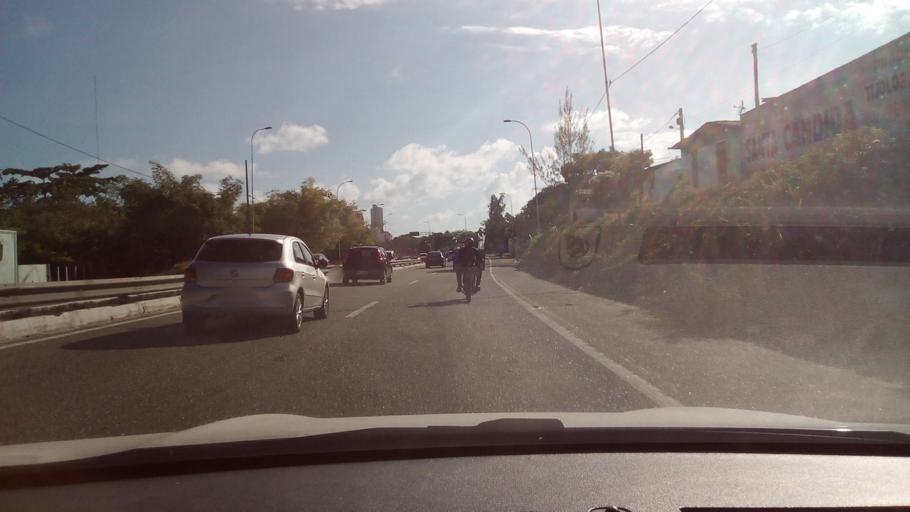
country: BR
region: Paraiba
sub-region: Joao Pessoa
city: Joao Pessoa
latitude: -7.1289
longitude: -34.8493
